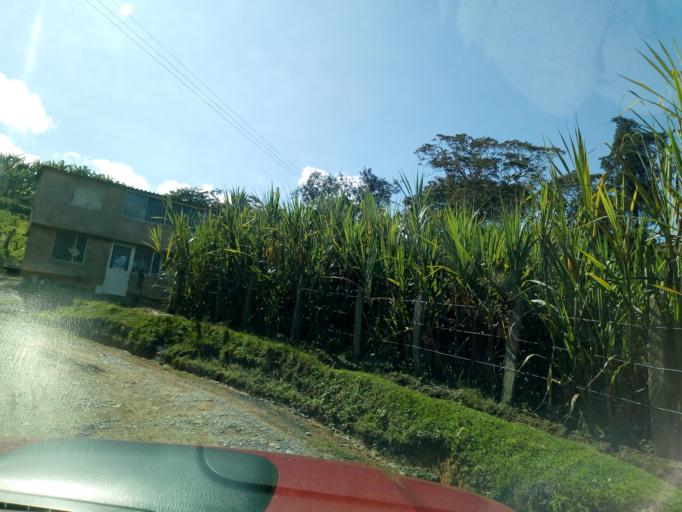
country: CO
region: Boyaca
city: Moniquira
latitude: 5.8913
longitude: -73.5254
